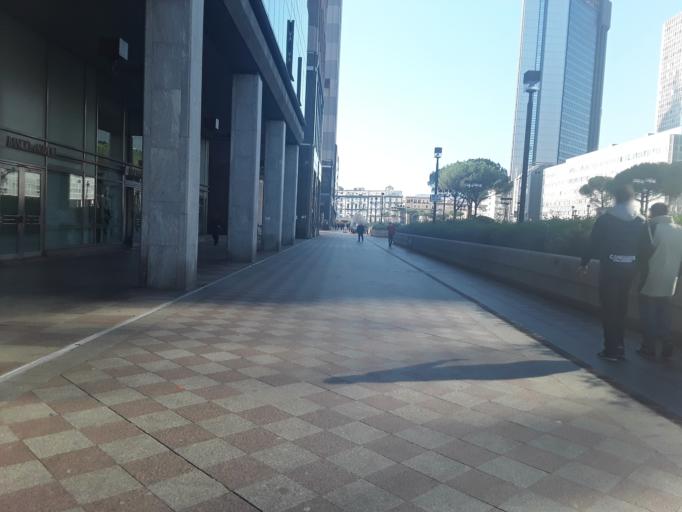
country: IT
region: Campania
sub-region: Provincia di Napoli
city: Napoli
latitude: 40.8566
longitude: 14.2804
